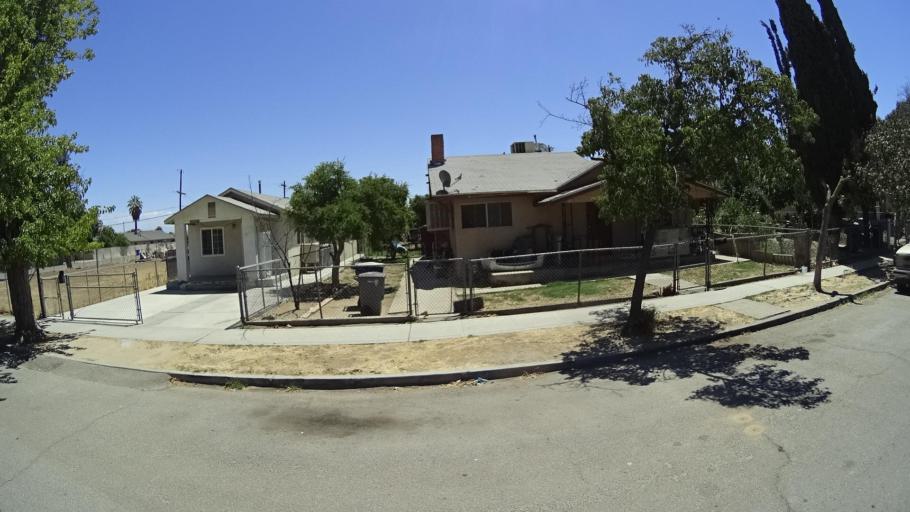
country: US
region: California
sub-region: Fresno County
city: Fresno
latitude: 36.7046
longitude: -119.7560
